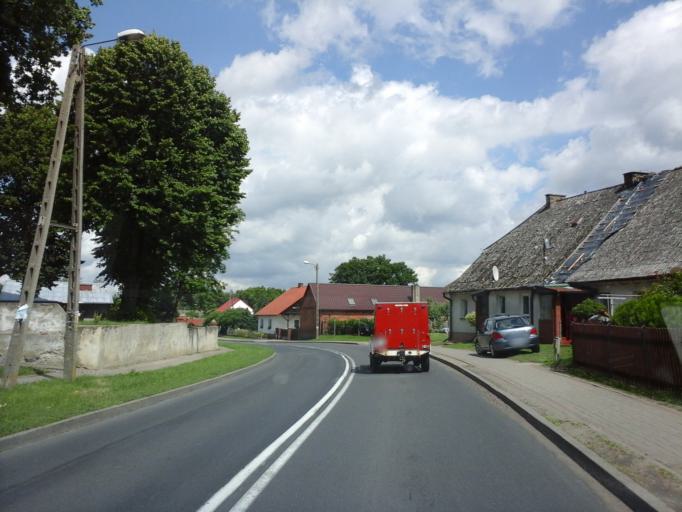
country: PL
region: Lubusz
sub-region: Powiat strzelecko-drezdenecki
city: Strzelce Krajenskie
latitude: 52.9008
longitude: 15.5950
